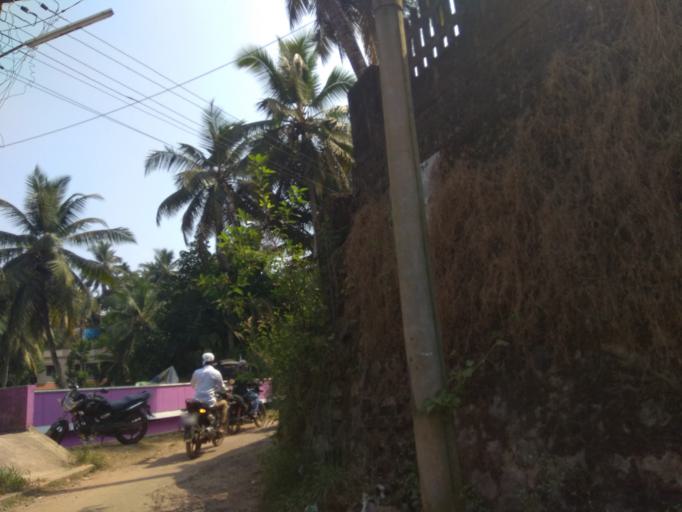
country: IN
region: Karnataka
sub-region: Dakshina Kannada
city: Mangalore
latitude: 12.9287
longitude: 74.8431
